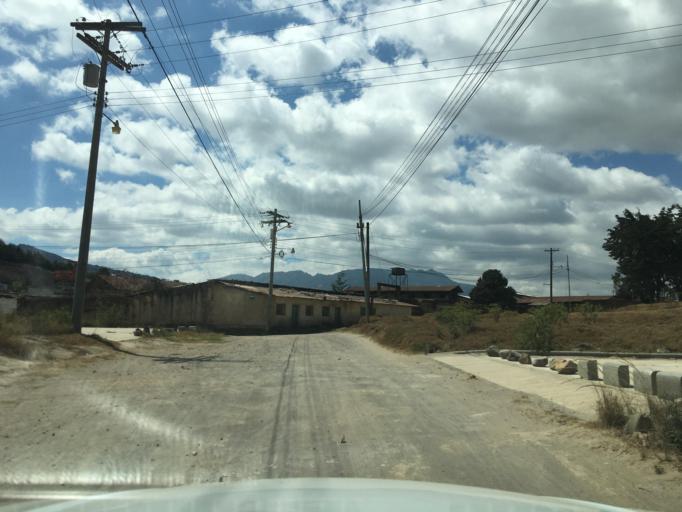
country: GT
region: Quetzaltenango
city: Quetzaltenango
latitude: 14.8428
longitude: -91.4965
